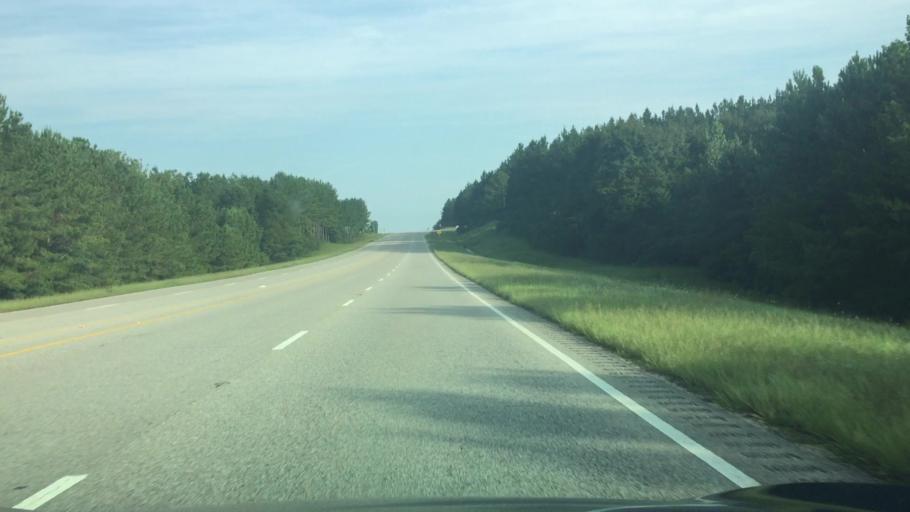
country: US
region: Alabama
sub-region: Butler County
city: Georgiana
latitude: 31.4789
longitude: -86.6743
